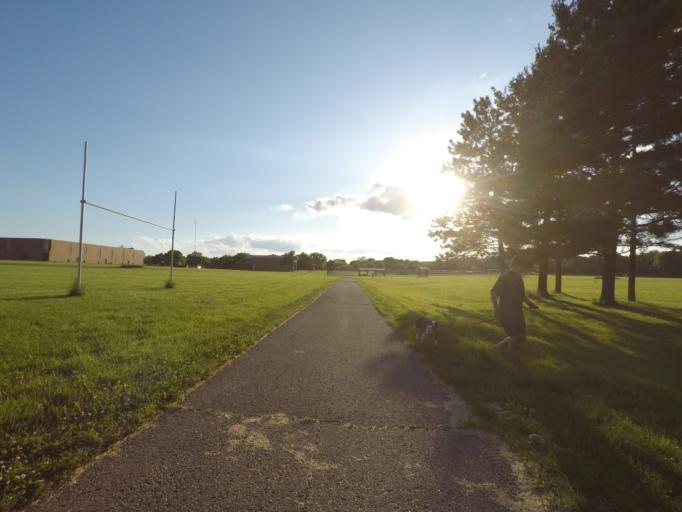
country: US
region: Wisconsin
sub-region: Dane County
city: Middleton
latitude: 43.0660
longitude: -89.4979
